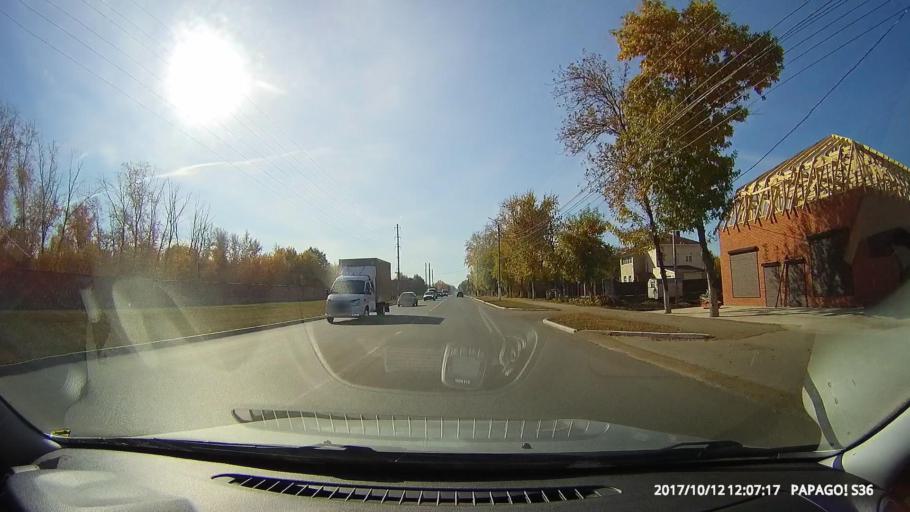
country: RU
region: Samara
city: Chapayevsk
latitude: 52.9680
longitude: 49.7022
